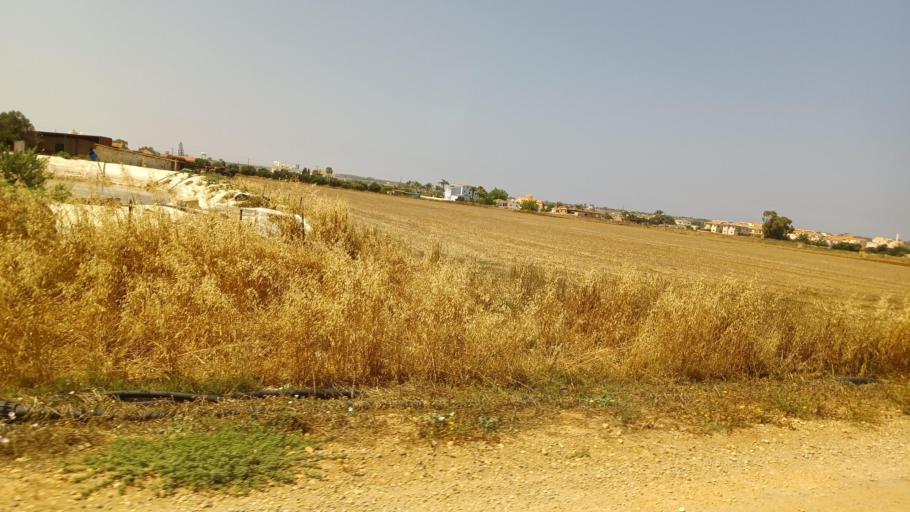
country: CY
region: Ammochostos
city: Liopetri
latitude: 34.9788
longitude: 33.8645
